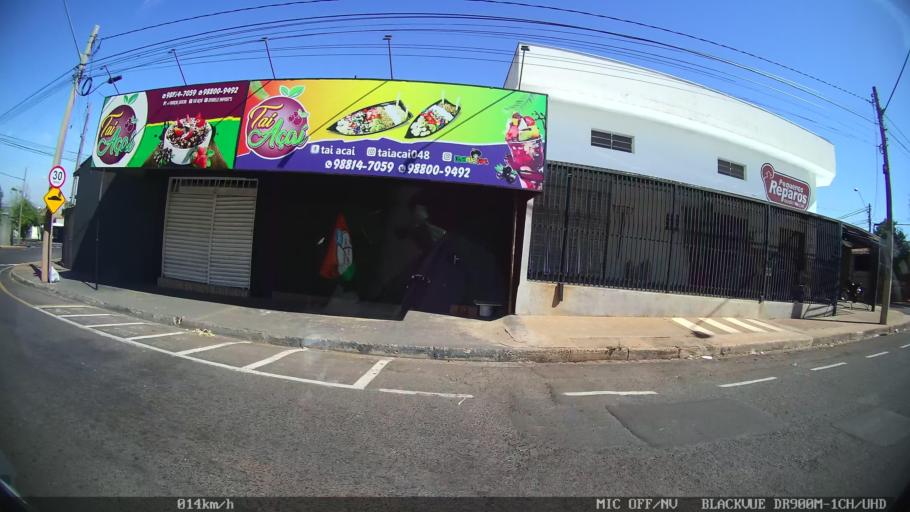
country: BR
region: Sao Paulo
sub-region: Sao Jose Do Rio Preto
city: Sao Jose do Rio Preto
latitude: -20.7502
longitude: -49.4070
